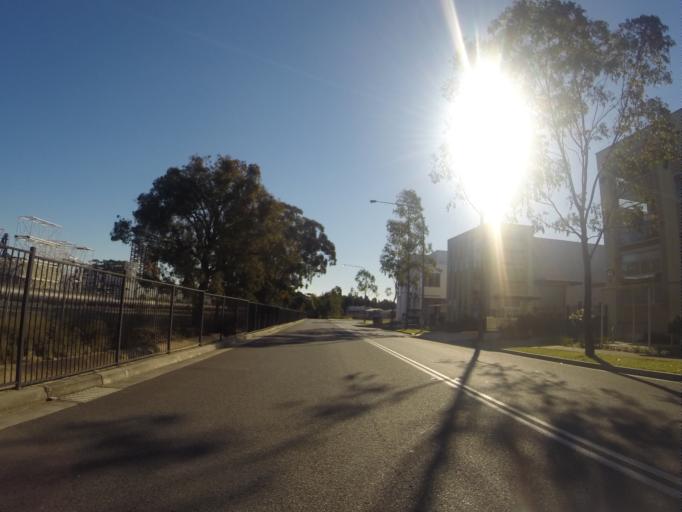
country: AU
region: New South Wales
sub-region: Bankstown
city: Regents Park
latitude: -33.8793
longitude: 151.0153
